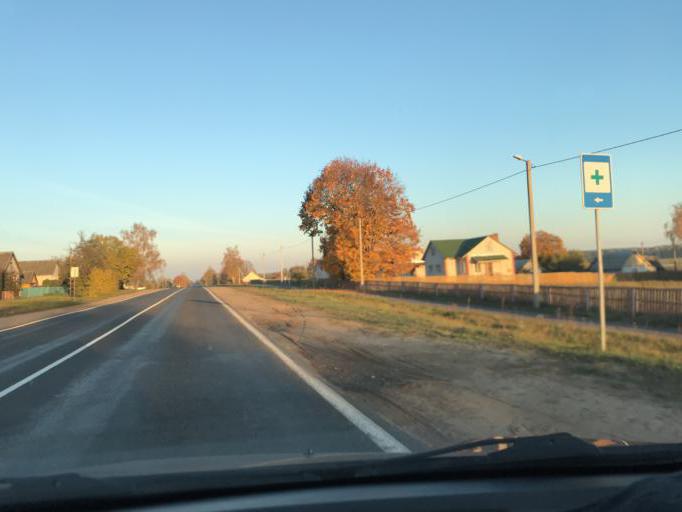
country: BY
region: Minsk
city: Staryya Darohi
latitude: 53.0540
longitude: 28.4120
